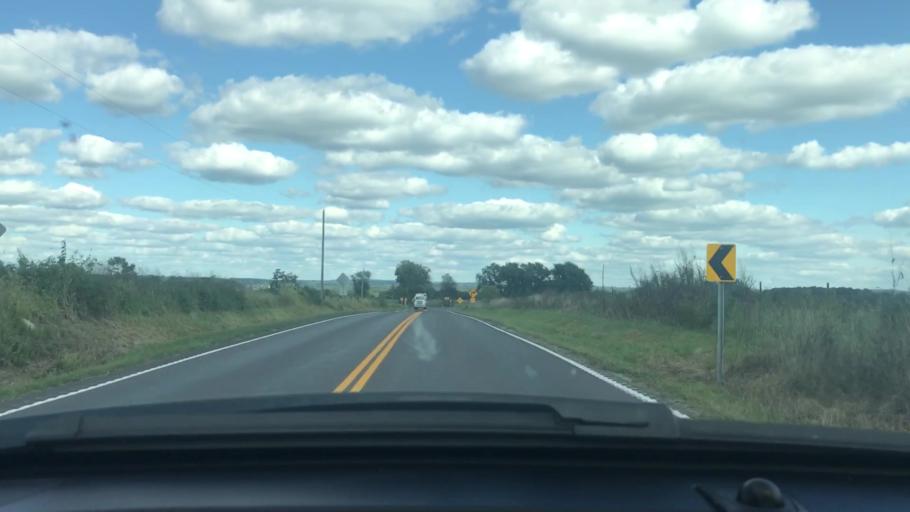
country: US
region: Missouri
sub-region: Wright County
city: Mountain Grove
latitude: 37.1653
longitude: -92.2659
